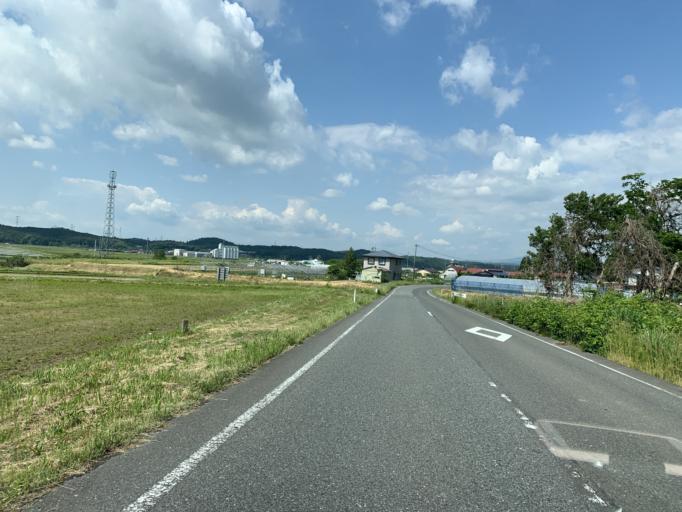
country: JP
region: Iwate
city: Ichinoseki
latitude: 38.8097
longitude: 140.9908
